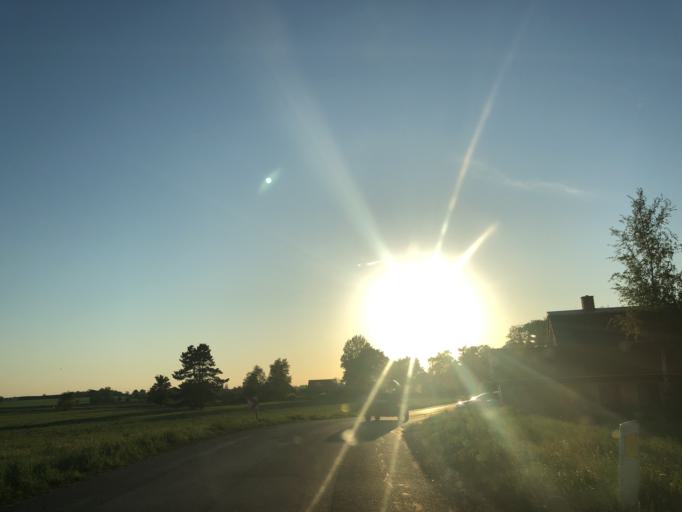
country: DK
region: Zealand
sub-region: Ringsted Kommune
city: Ringsted
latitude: 55.4067
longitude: 11.8404
